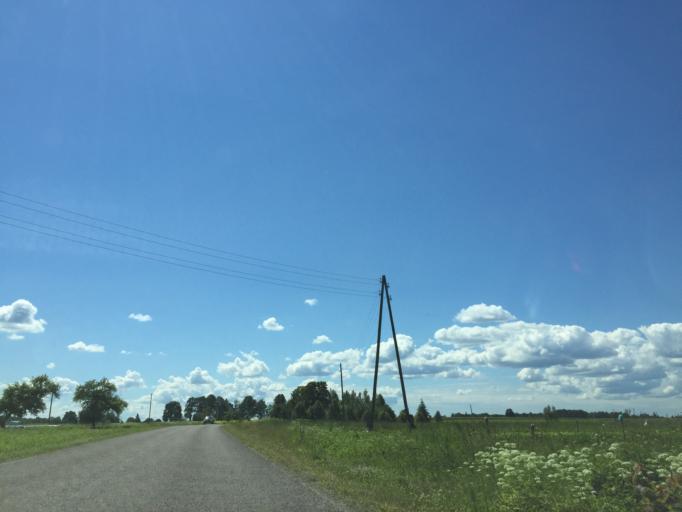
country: LV
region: Sigulda
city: Sigulda
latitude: 57.1986
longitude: 24.9470
